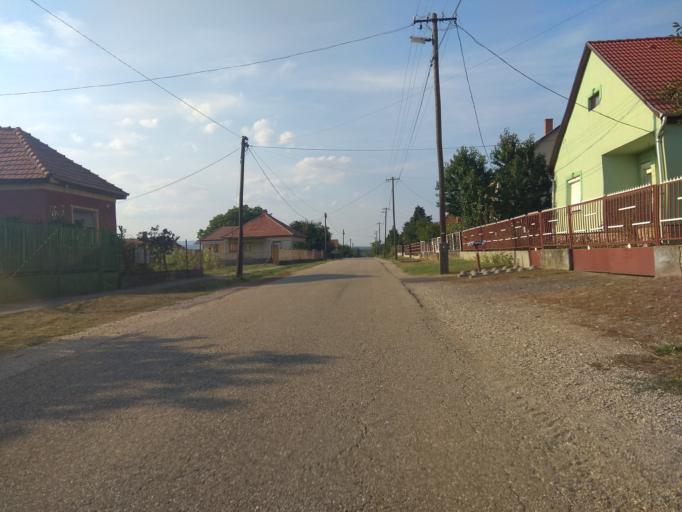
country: HU
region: Borsod-Abauj-Zemplen
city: Harsany
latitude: 47.9157
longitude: 20.7409
